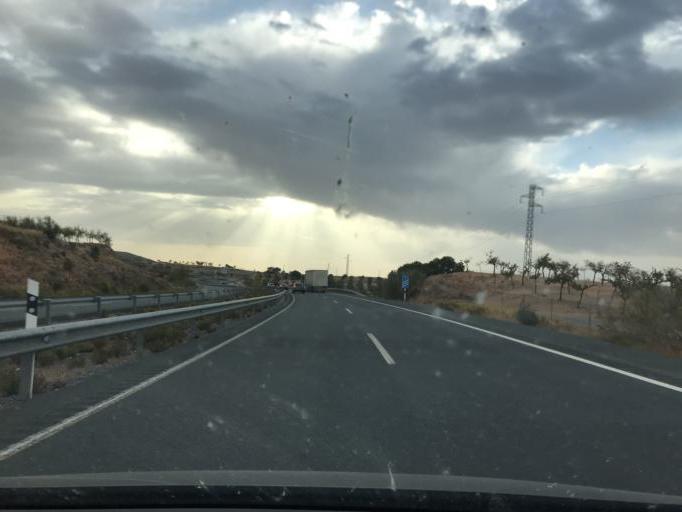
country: ES
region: Andalusia
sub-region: Provincia de Granada
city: Gor
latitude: 37.3915
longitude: -3.0034
